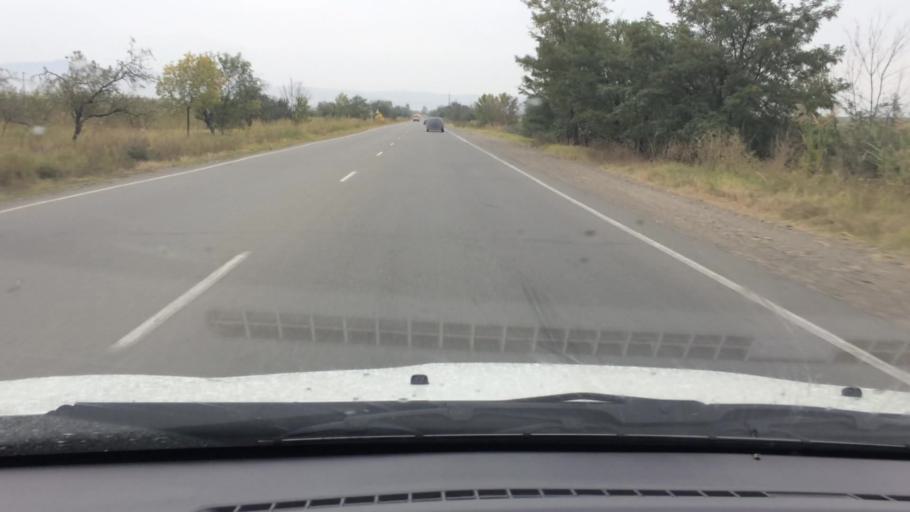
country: GE
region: Kvemo Kartli
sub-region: Marneuli
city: Marneuli
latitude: 41.5280
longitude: 44.7771
